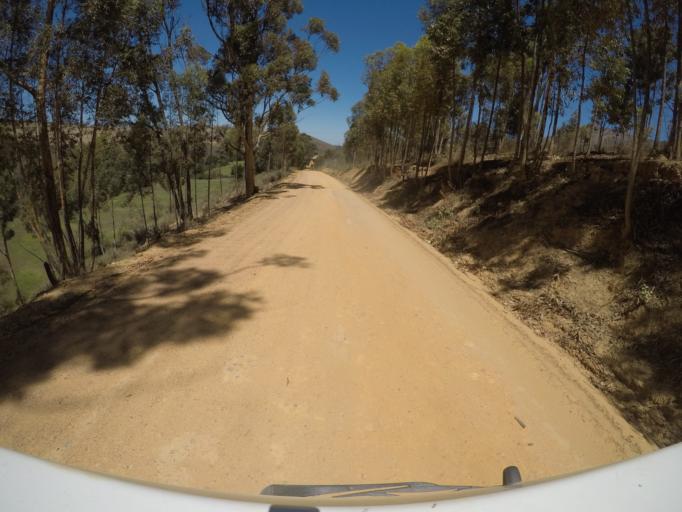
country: ZA
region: Western Cape
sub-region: Overberg District Municipality
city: Caledon
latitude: -34.1984
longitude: 19.2211
